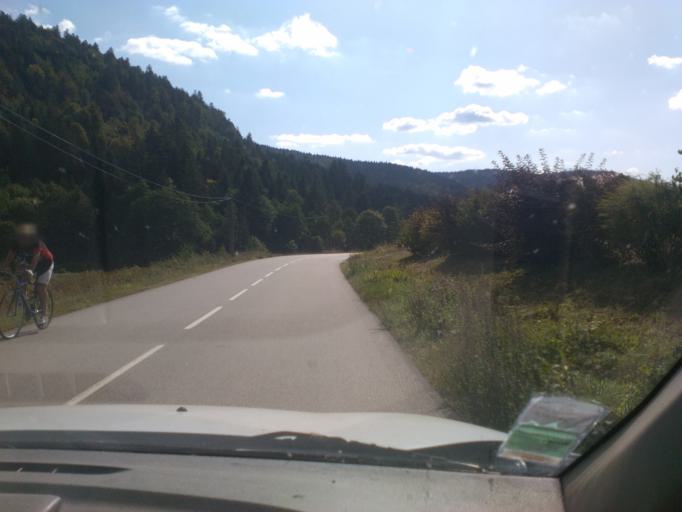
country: FR
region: Lorraine
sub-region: Departement des Vosges
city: Gerardmer
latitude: 48.0438
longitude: 6.8652
